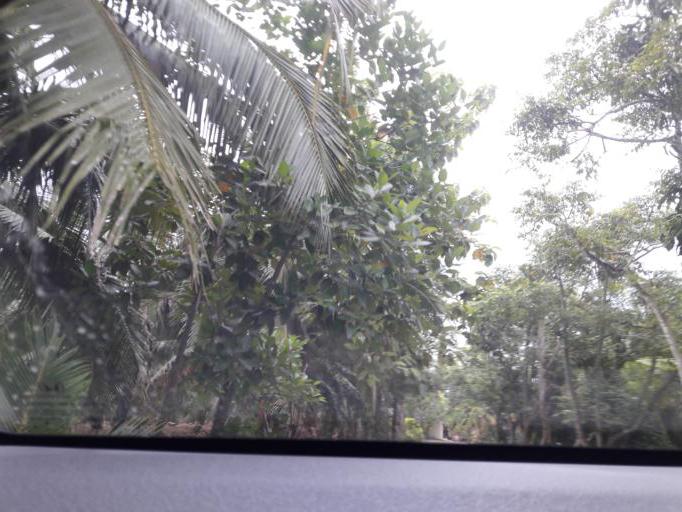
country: TH
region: Ratchaburi
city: Damnoen Saduak
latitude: 13.5626
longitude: 99.9985
